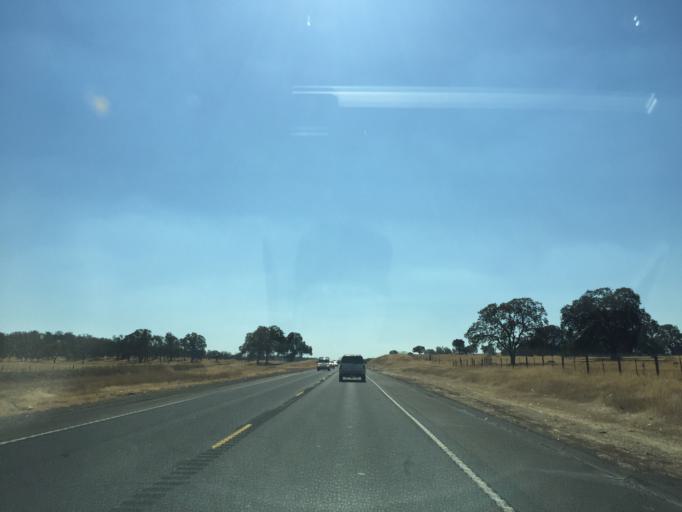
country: US
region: California
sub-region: Tuolumne County
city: Jamestown
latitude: 37.8523
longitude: -120.5093
